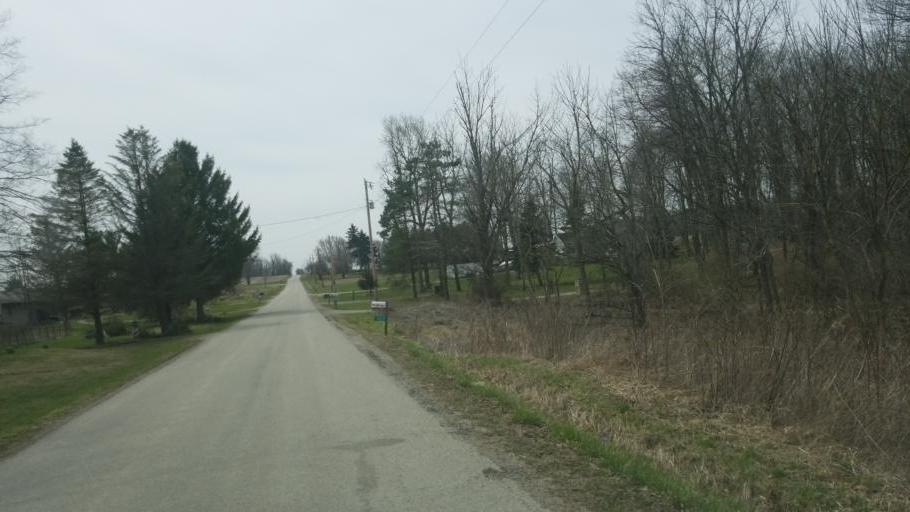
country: US
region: Ohio
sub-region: Knox County
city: Centerburg
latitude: 40.3301
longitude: -82.6477
